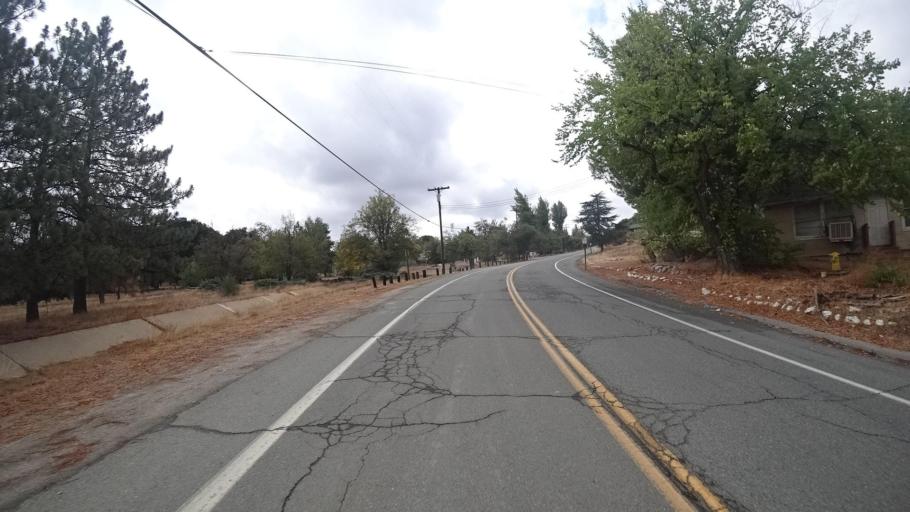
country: US
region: California
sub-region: San Diego County
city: Campo
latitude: 32.6042
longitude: -116.4705
